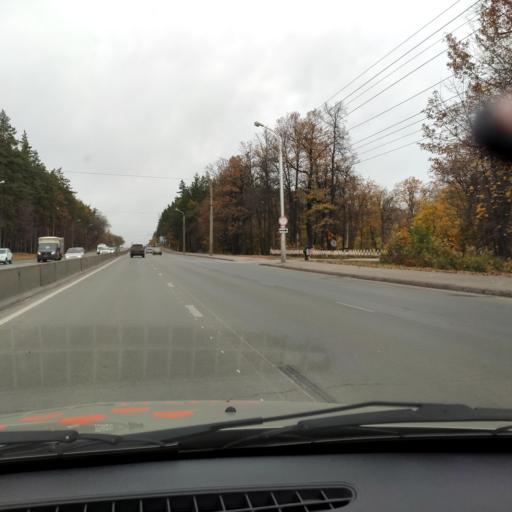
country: RU
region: Bashkortostan
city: Ufa
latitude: 54.7345
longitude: 56.0265
